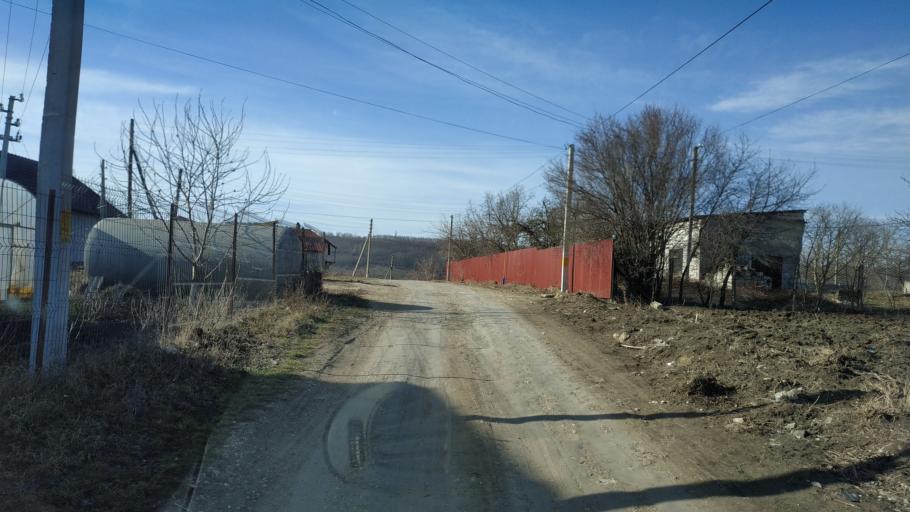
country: MD
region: Chisinau
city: Vatra
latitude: 47.0206
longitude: 28.6489
